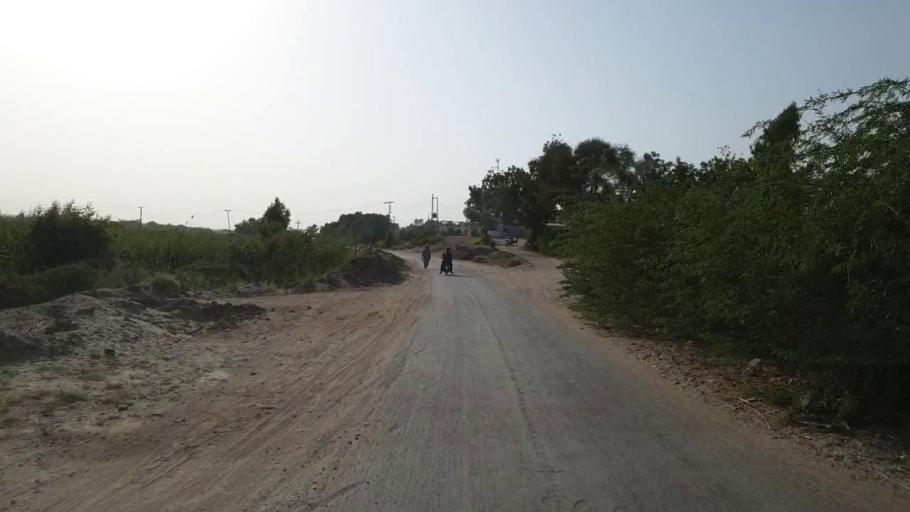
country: PK
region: Sindh
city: Jam Sahib
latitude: 26.4345
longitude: 68.8747
